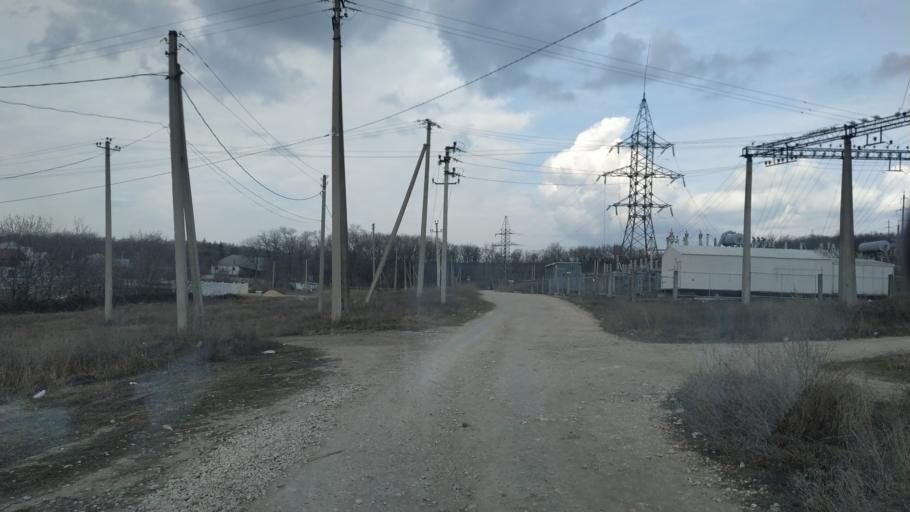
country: MD
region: Anenii Noi
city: Anenii Noi
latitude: 46.8928
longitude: 29.2809
